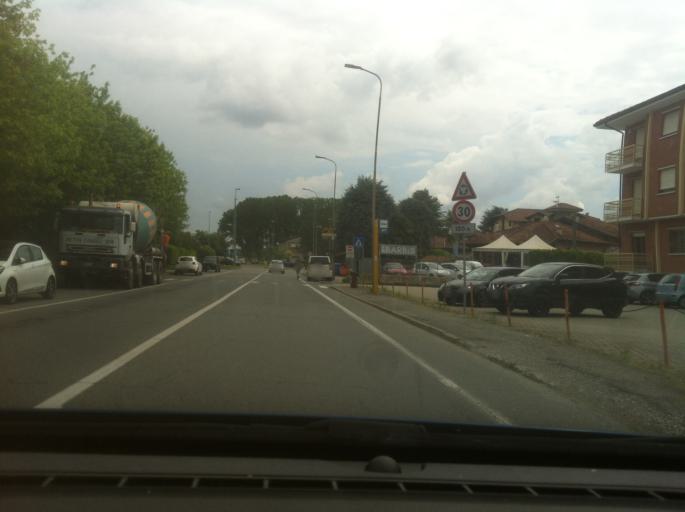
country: IT
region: Piedmont
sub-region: Provincia di Torino
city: Strambino
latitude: 45.3796
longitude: 7.8818
